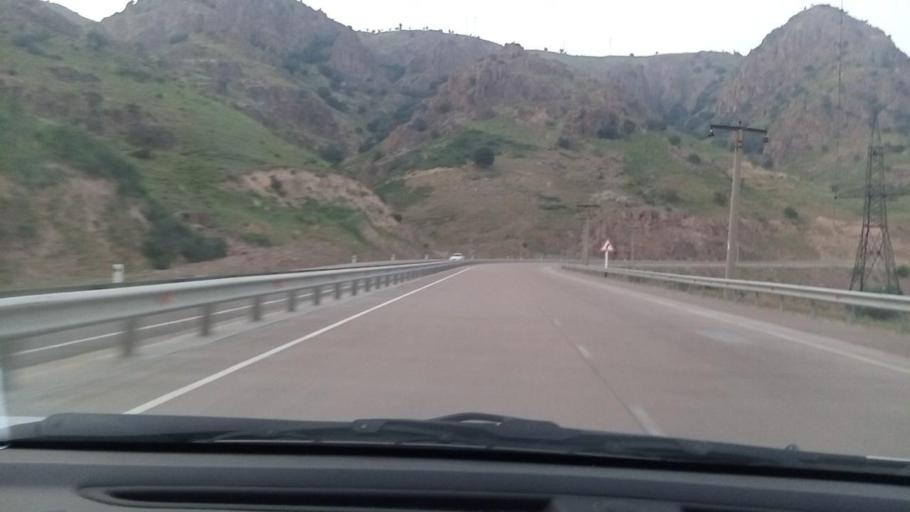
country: UZ
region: Toshkent
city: Angren
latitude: 41.1352
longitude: 70.3730
